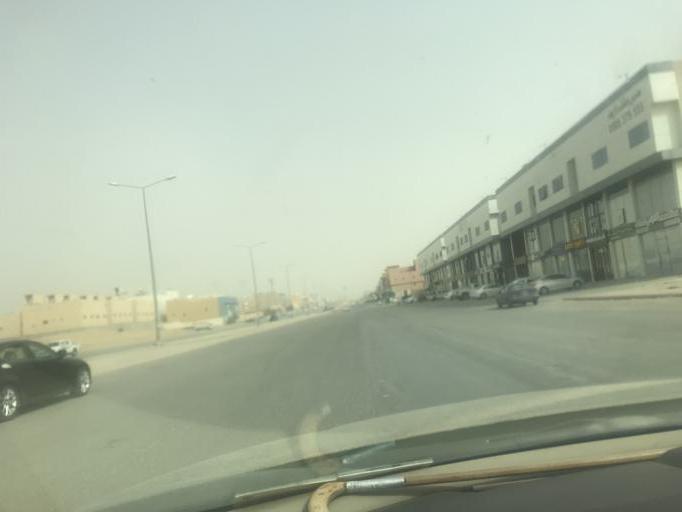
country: SA
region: Ar Riyad
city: Riyadh
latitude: 24.8044
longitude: 46.6037
